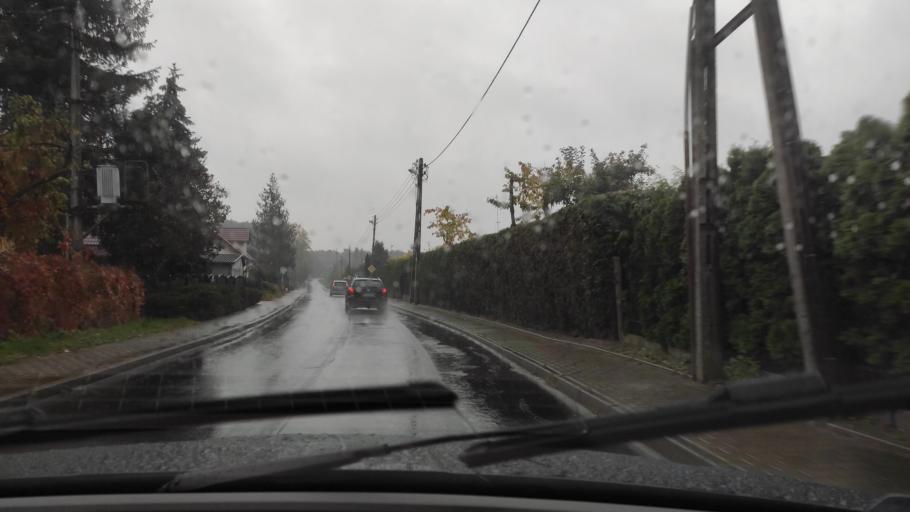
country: PL
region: Greater Poland Voivodeship
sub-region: Powiat poznanski
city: Kornik
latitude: 52.2242
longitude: 17.0956
